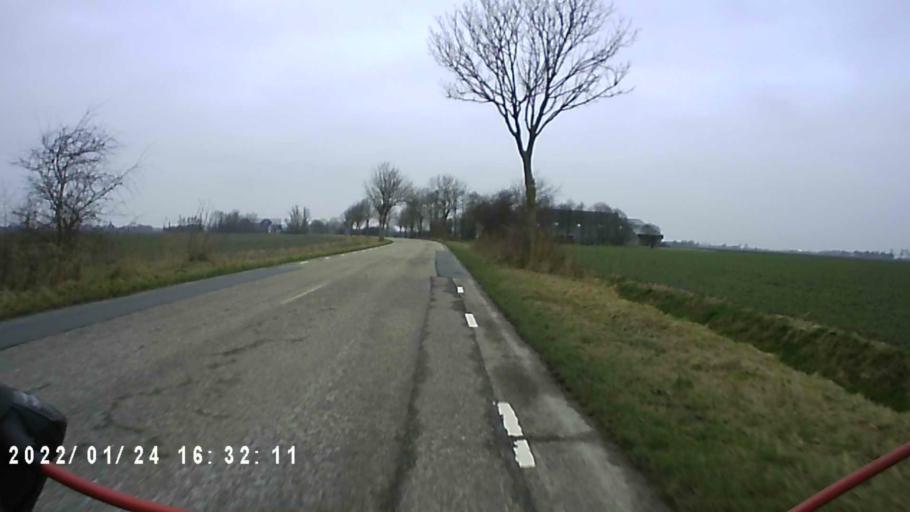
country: NL
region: Groningen
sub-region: Gemeente Zuidhorn
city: Oldehove
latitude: 53.3702
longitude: 6.4204
